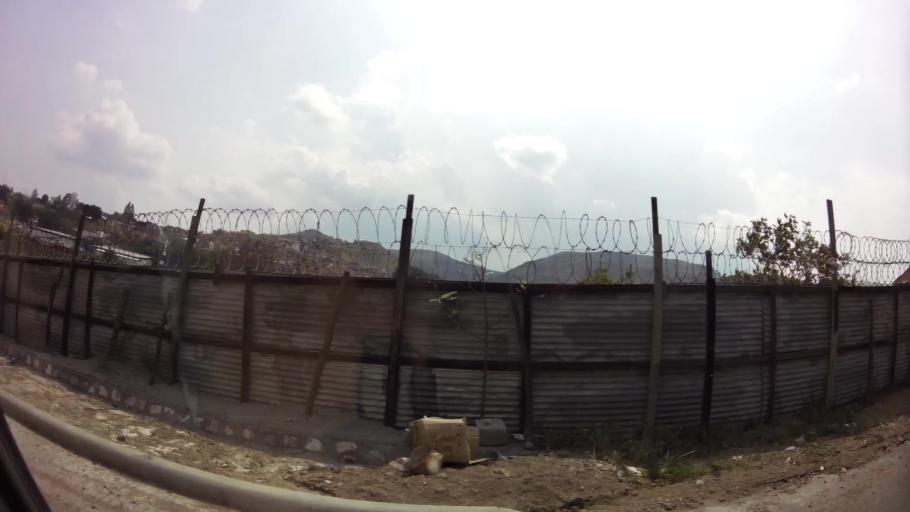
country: HN
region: Francisco Morazan
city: El Lolo
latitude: 14.1217
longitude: -87.2237
